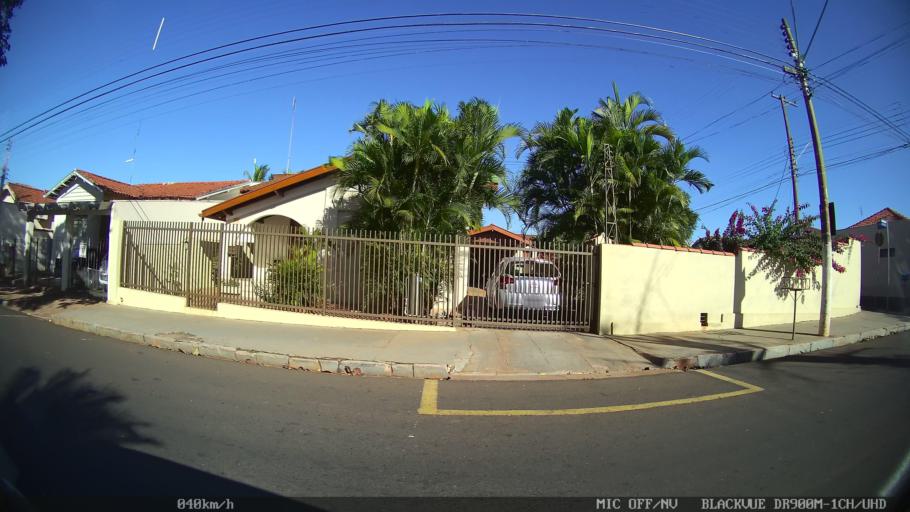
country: BR
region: Sao Paulo
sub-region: Olimpia
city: Olimpia
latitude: -20.7460
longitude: -48.9137
